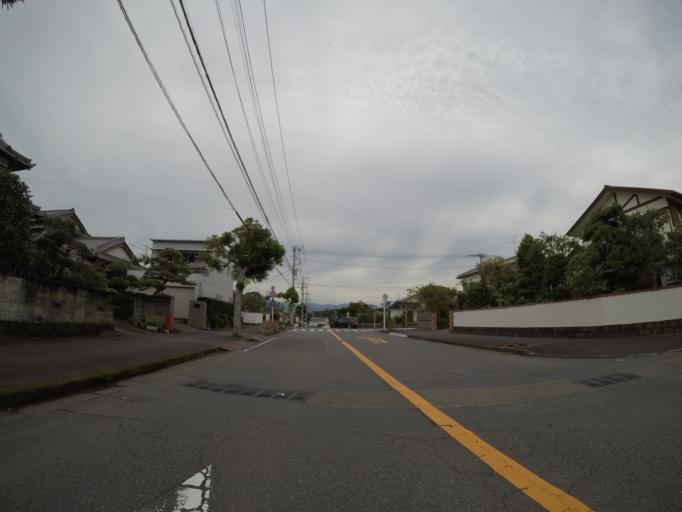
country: JP
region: Shizuoka
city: Fuji
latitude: 35.1809
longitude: 138.7100
